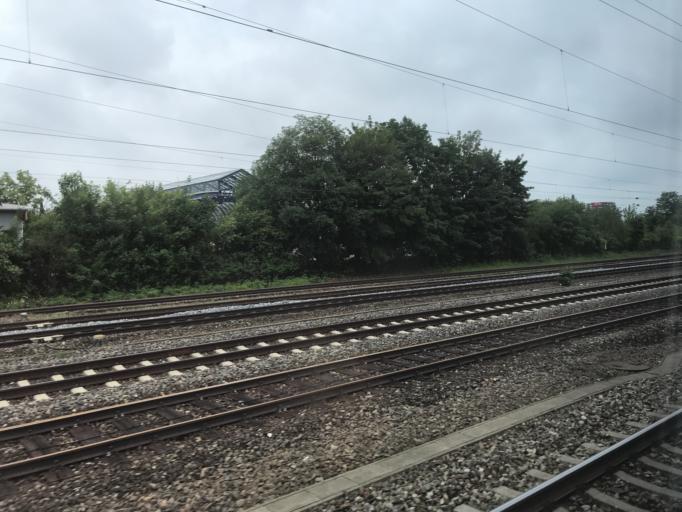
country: DE
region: Bavaria
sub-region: Upper Bavaria
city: Pasing
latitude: 48.1465
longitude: 11.4776
